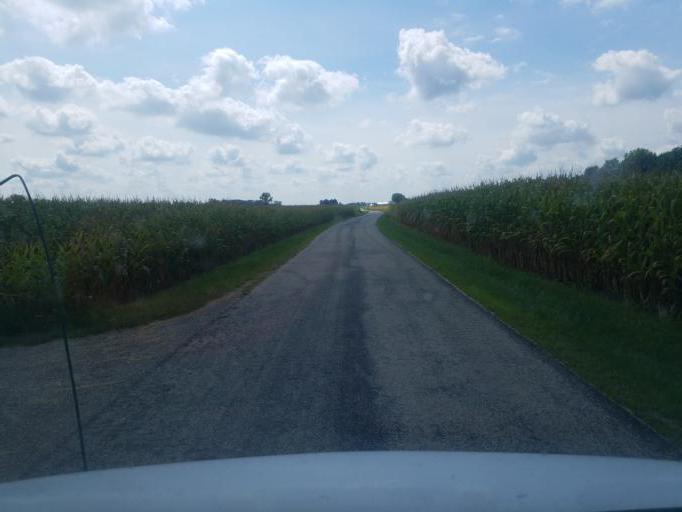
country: US
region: Ohio
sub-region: Marion County
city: Prospect
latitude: 40.4368
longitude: -83.1415
